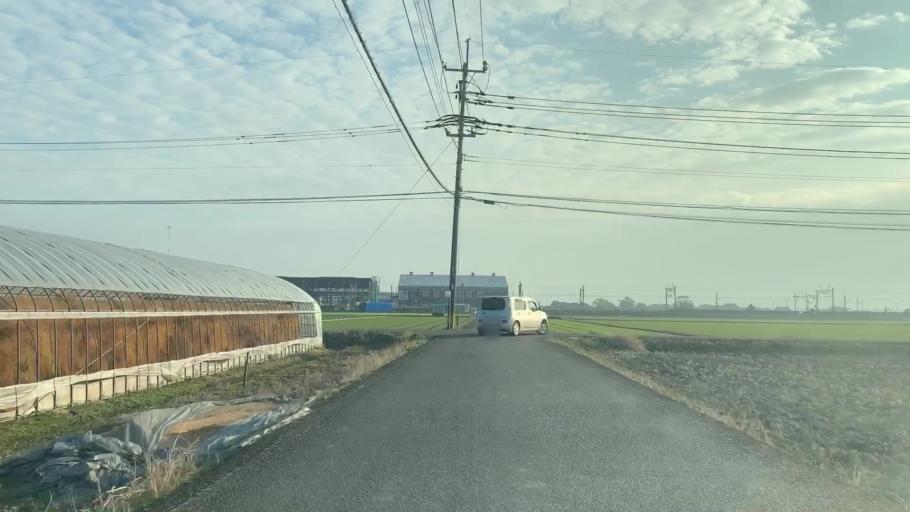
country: JP
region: Saga Prefecture
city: Saga-shi
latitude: 33.2611
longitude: 130.2603
